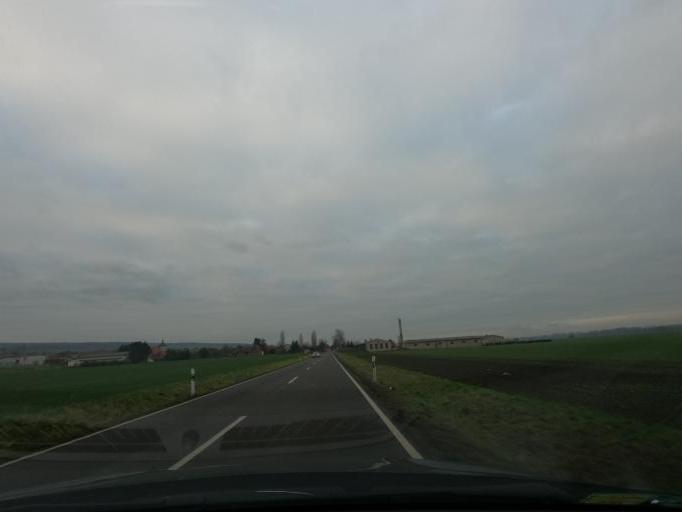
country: DE
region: Lower Saxony
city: Roklum
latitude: 52.0385
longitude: 10.7530
